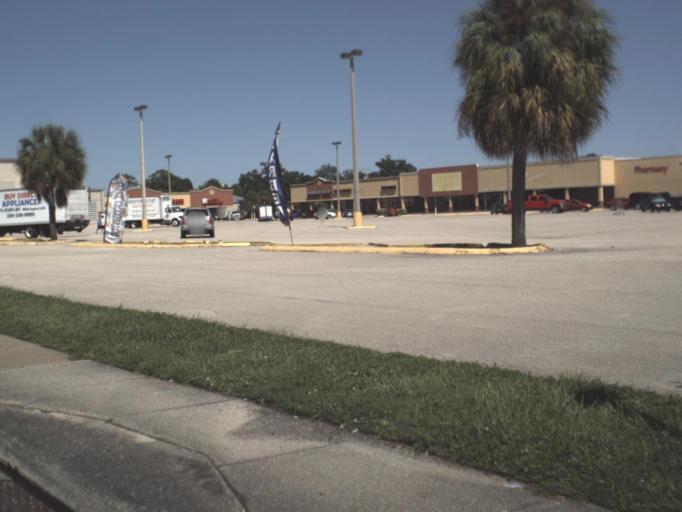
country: US
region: Florida
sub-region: Lee County
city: Pine Manor
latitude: 26.6047
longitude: -81.8718
